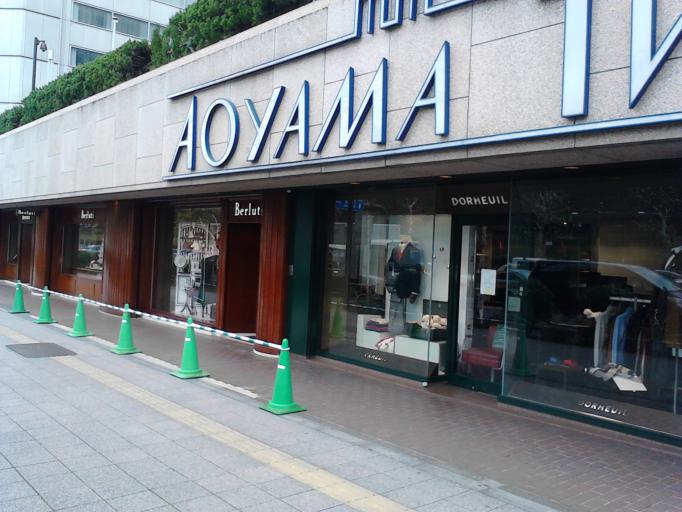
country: JP
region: Tokyo
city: Tokyo
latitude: 35.6727
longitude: 139.7245
